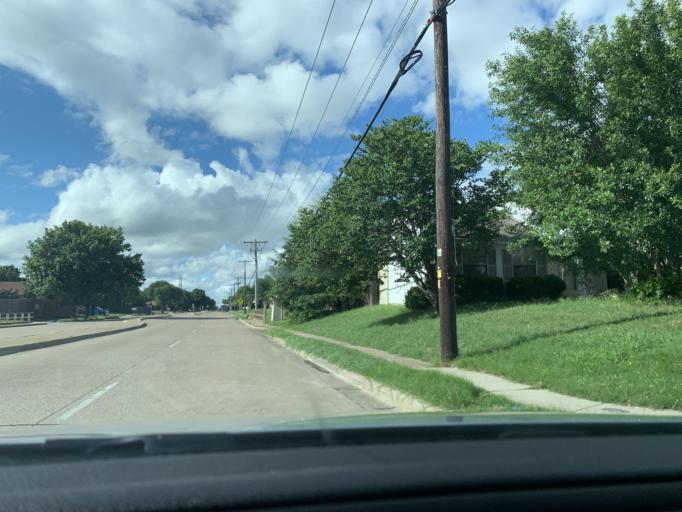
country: US
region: Texas
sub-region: Dallas County
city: Cedar Hill
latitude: 32.6515
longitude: -97.0278
